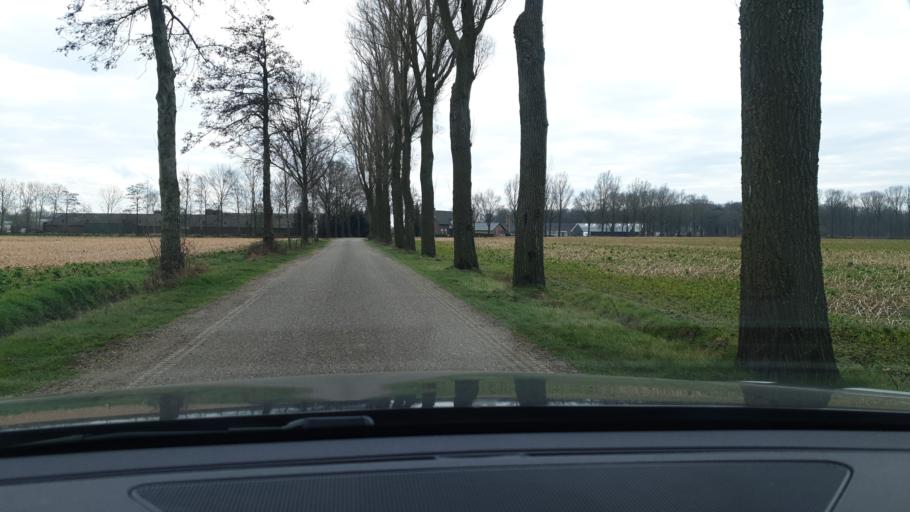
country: NL
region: North Brabant
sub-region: Gemeente Eersel
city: Eersel
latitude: 51.4069
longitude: 5.2765
